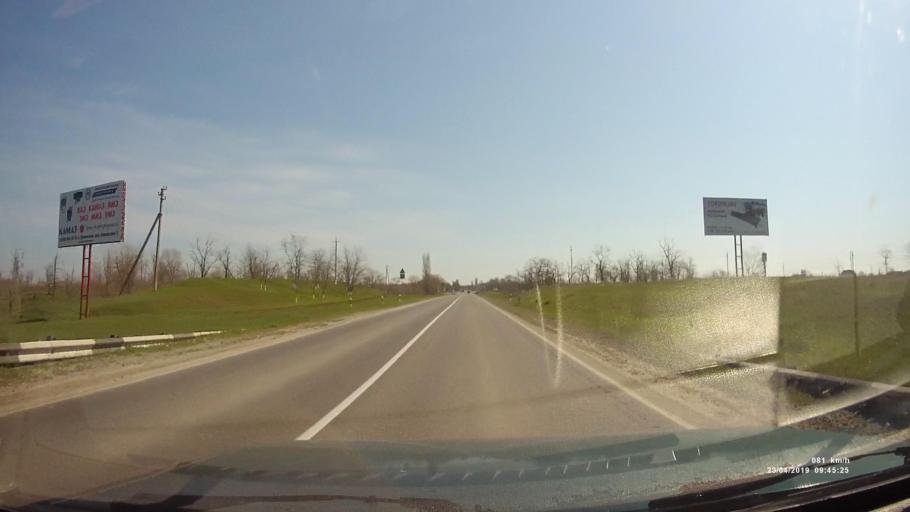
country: RU
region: Rostov
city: Orlovskiy
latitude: 46.8832
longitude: 42.0303
